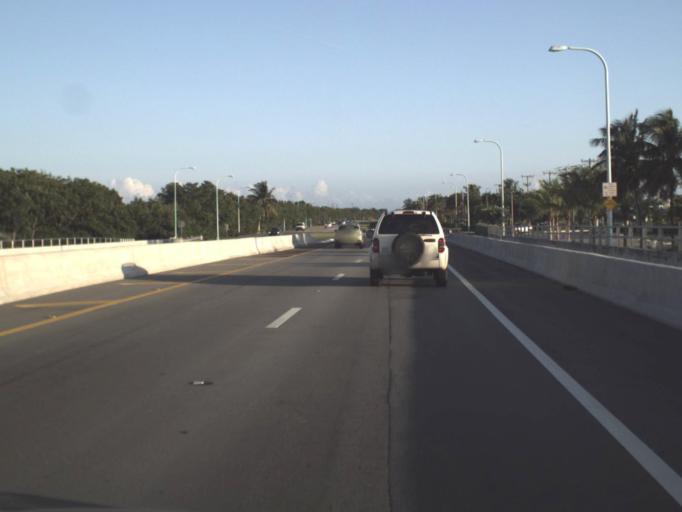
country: US
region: Florida
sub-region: Miami-Dade County
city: Key Biscayne
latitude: 25.7283
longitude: -80.1565
